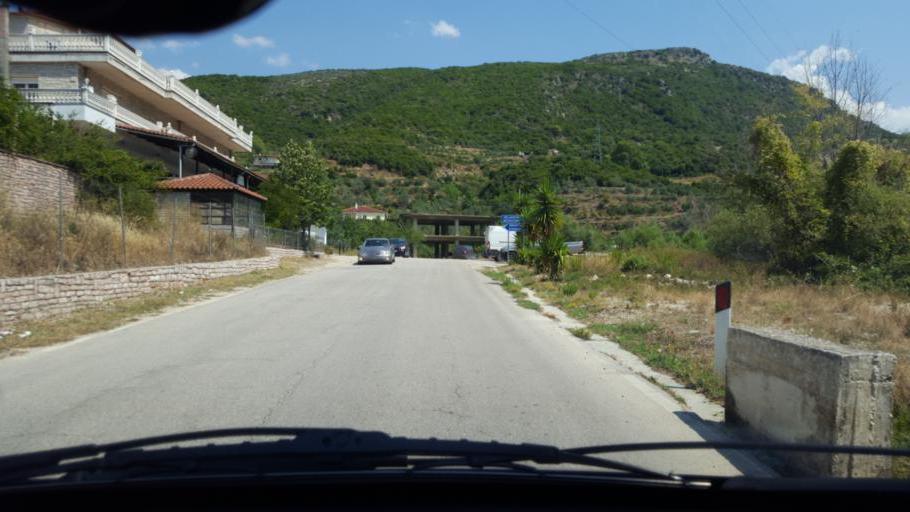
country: AL
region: Vlore
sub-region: Rrethi i Delvines
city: Mesopotam
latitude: 39.9170
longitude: 20.1352
